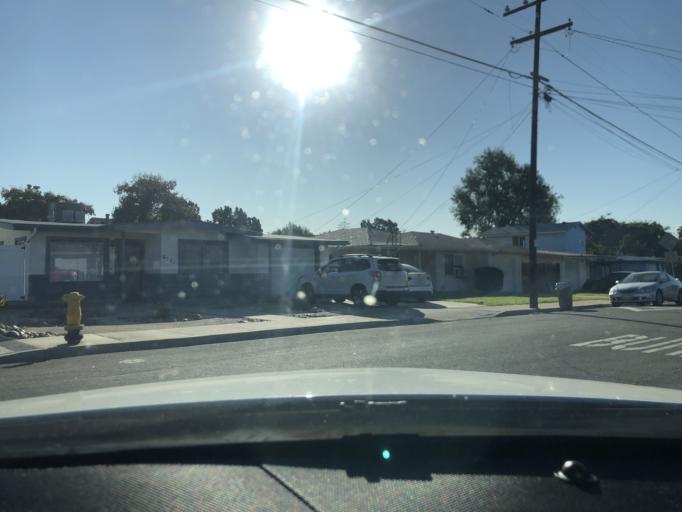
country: US
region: California
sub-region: San Diego County
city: Lemon Grove
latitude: 32.7424
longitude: -117.0584
